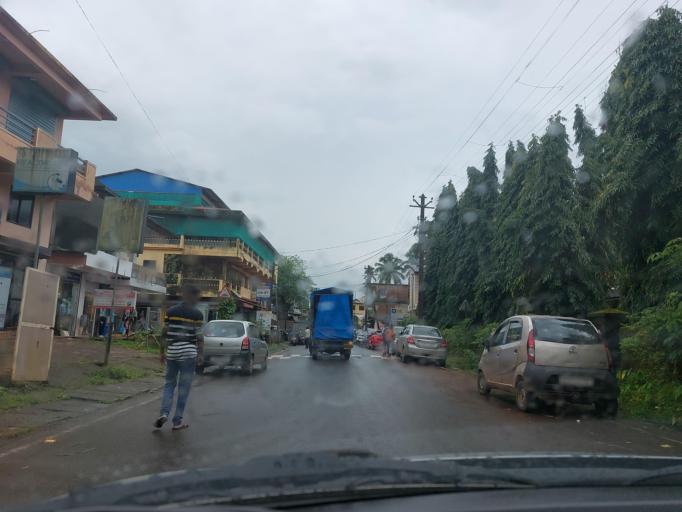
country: IN
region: Goa
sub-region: North Goa
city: Valpoy
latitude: 15.5329
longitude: 74.1370
